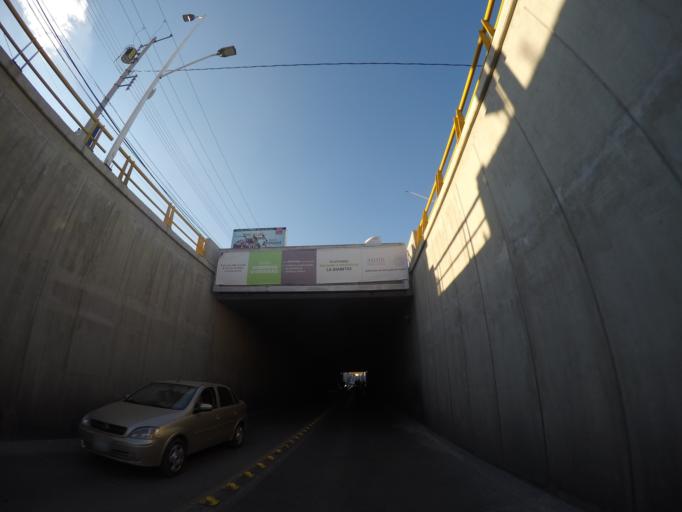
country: MX
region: San Luis Potosi
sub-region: San Luis Potosi
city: San Luis Potosi
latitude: 22.1648
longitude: -101.0011
